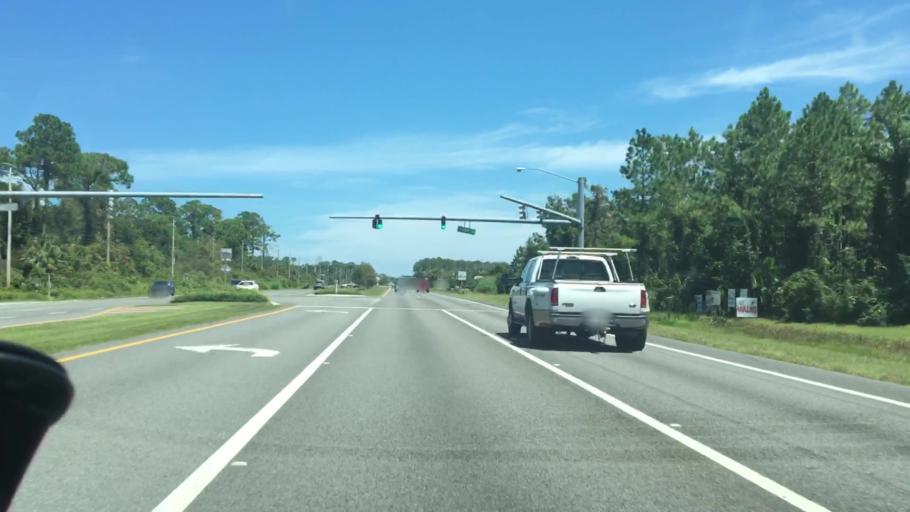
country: US
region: Florida
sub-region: Flagler County
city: Flagler Beach
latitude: 29.4768
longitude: -81.1544
